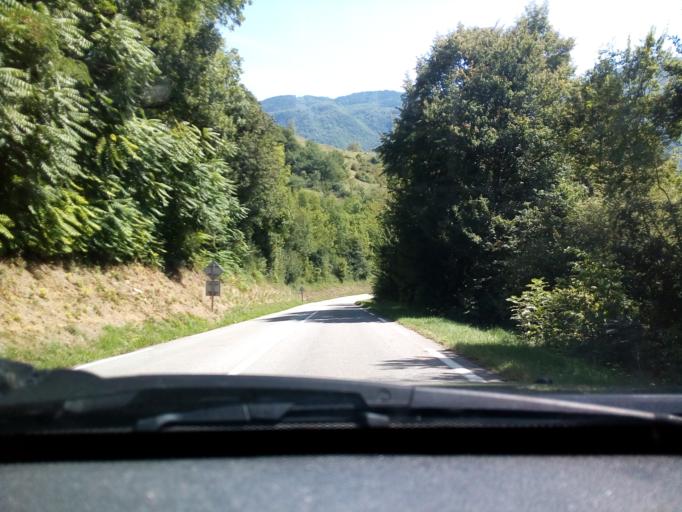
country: FR
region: Rhone-Alpes
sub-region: Departement de l'Isere
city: Vizille
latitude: 45.0915
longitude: 5.7776
